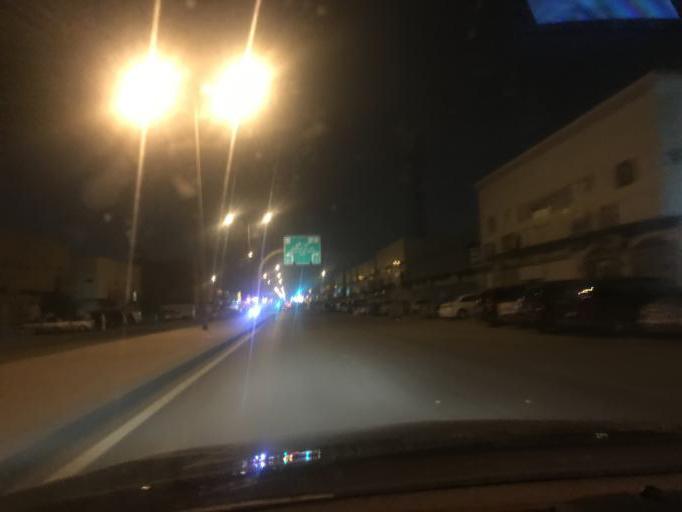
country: SA
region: Ar Riyad
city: Riyadh
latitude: 24.7639
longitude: 46.7966
